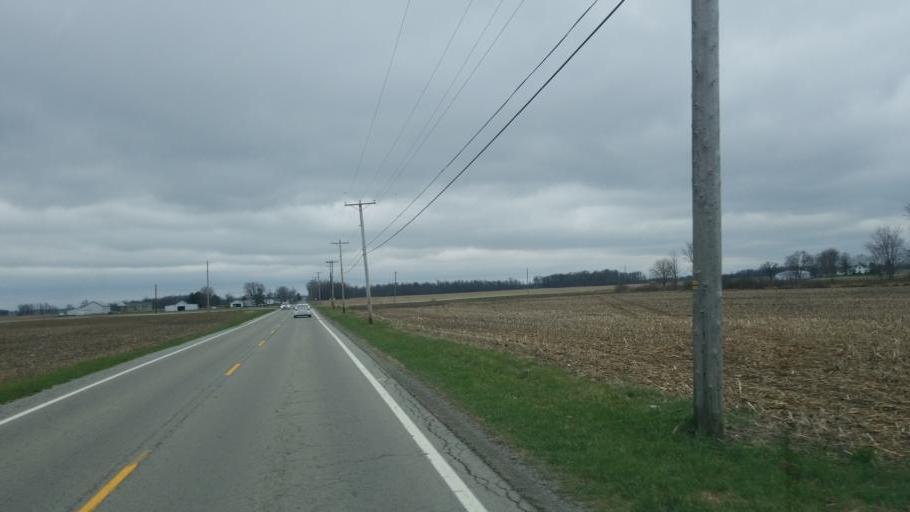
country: US
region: Ohio
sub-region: Hardin County
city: Kenton
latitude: 40.7041
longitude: -83.5731
